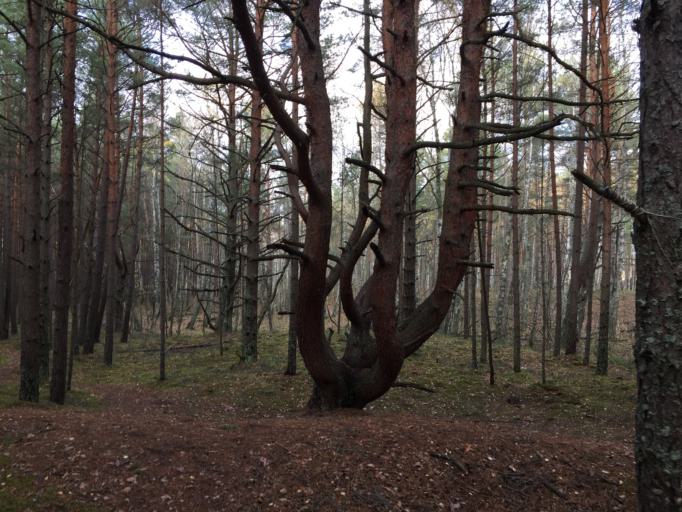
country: LV
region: Carnikava
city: Carnikava
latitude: 57.1514
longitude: 24.2580
